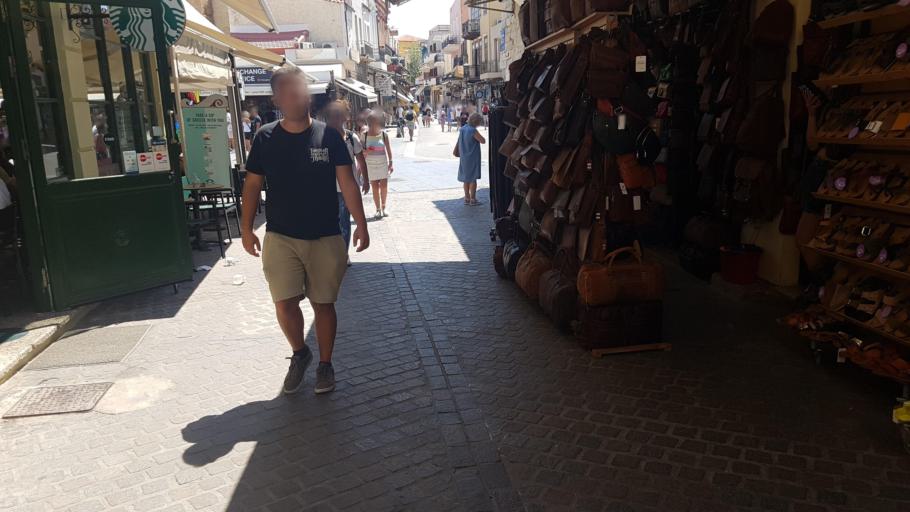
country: GR
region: Crete
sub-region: Nomos Chanias
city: Chania
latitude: 35.5104
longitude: 24.0035
